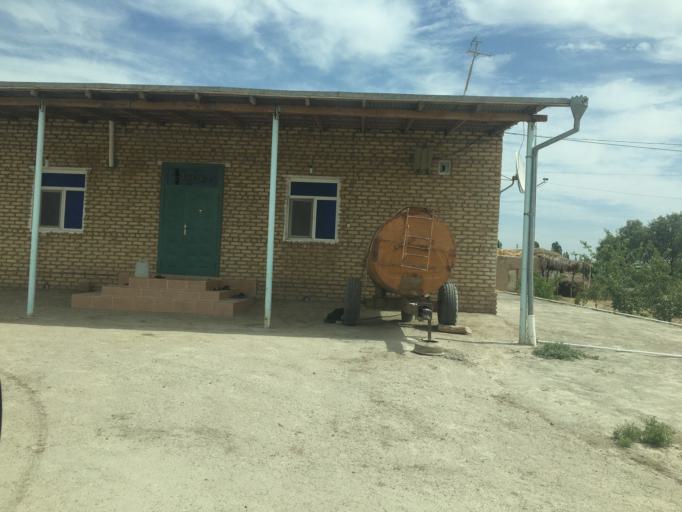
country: TM
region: Dasoguz
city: Tagta
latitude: 41.6040
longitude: 59.8434
